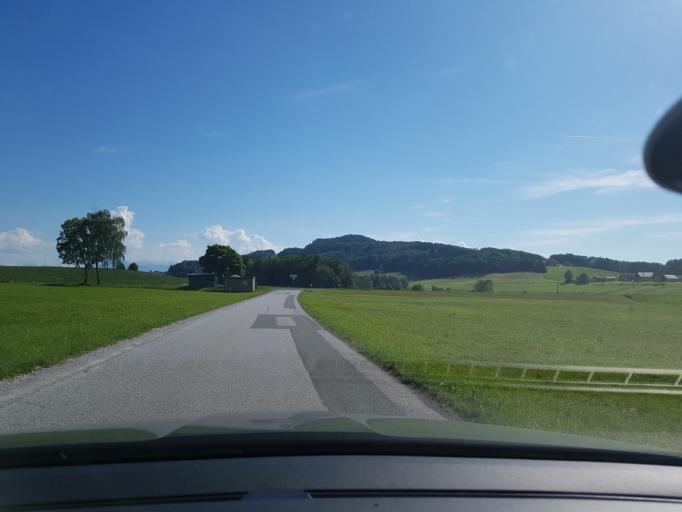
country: AT
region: Salzburg
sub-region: Politischer Bezirk Salzburg-Umgebung
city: Schleedorf
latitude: 47.9702
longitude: 13.1322
